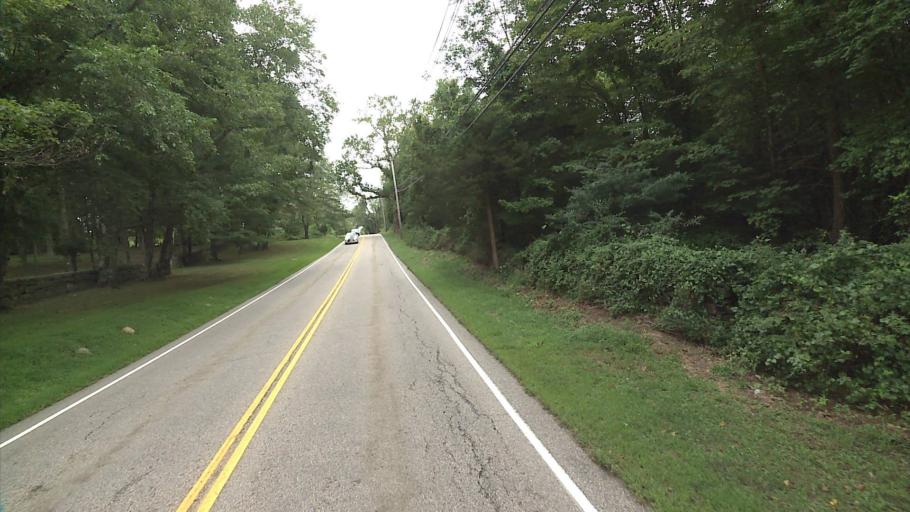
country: US
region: Connecticut
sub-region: Middlesex County
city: Essex Village
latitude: 41.3586
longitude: -72.3421
